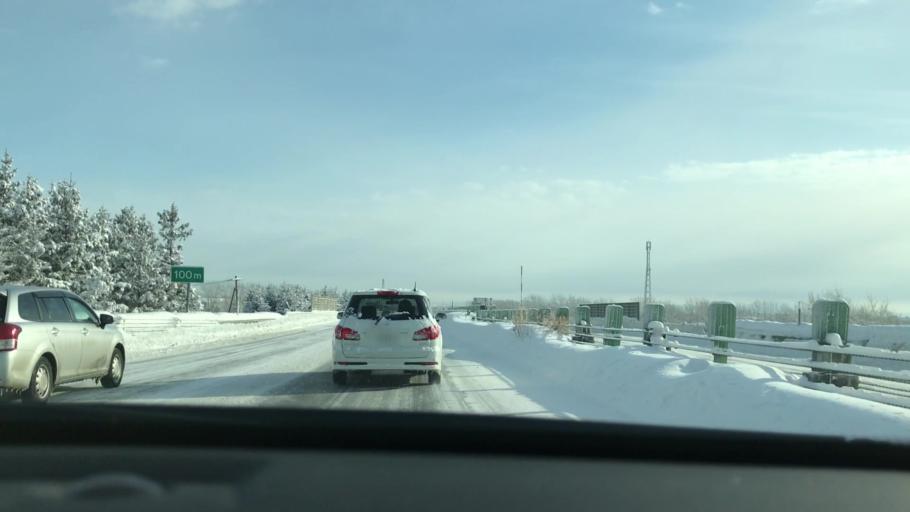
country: JP
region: Hokkaido
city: Sapporo
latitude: 43.0863
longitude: 141.4483
